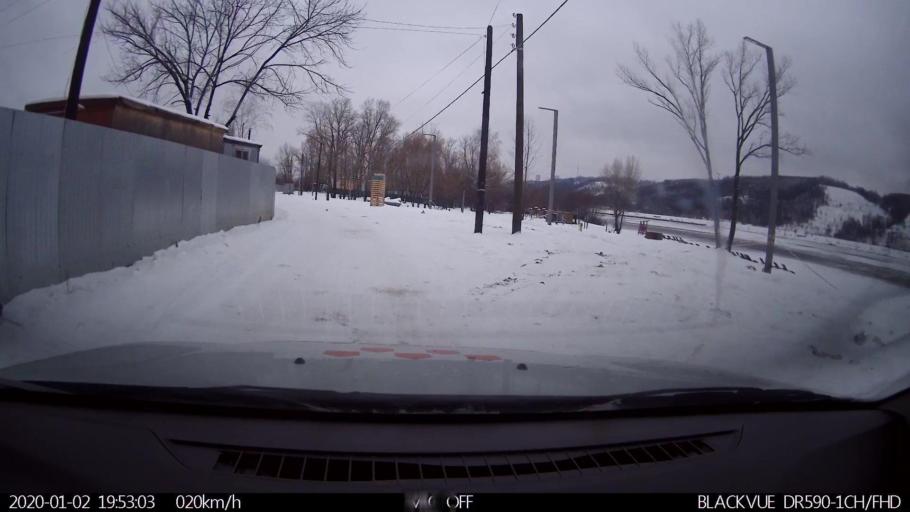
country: RU
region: Nizjnij Novgorod
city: Nizhniy Novgorod
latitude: 56.2725
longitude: 43.9597
